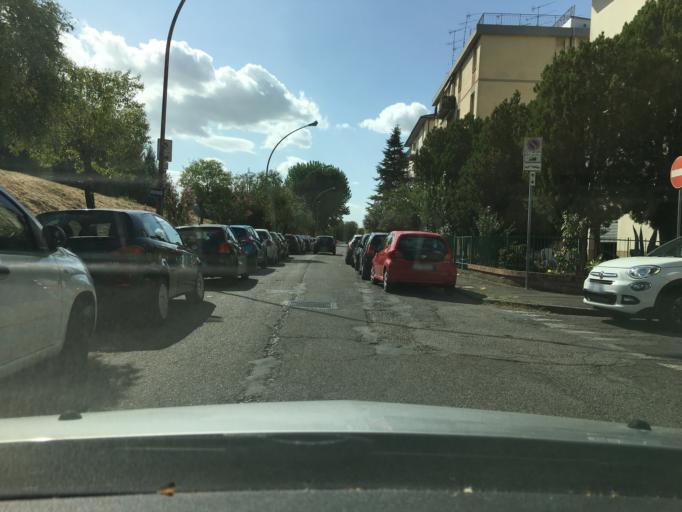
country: IT
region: Tuscany
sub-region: Province of Florence
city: Castelfiorentino
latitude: 43.6029
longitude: 10.9686
